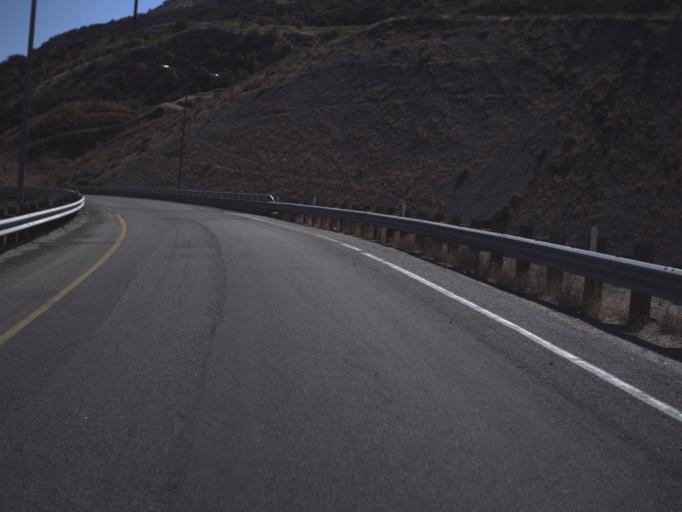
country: US
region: Utah
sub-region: Box Elder County
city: Brigham City
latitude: 41.4997
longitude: -111.9935
